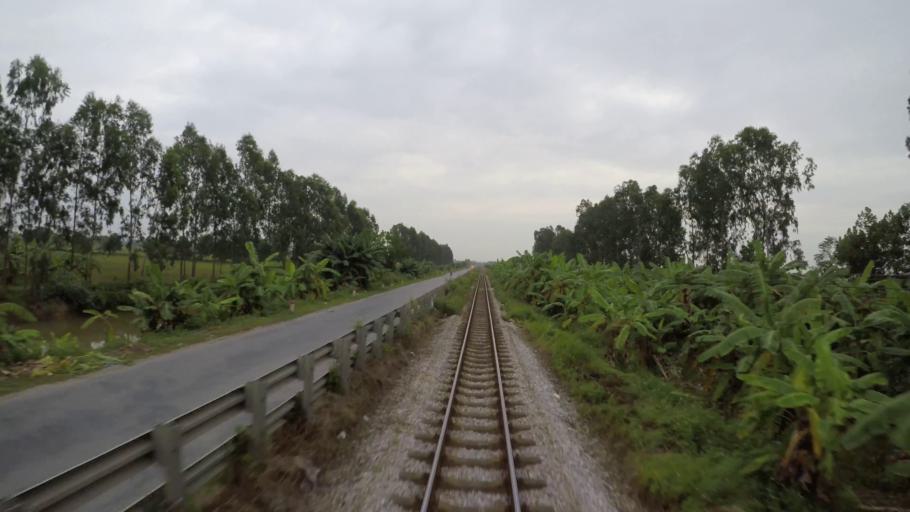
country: VN
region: Hung Yen
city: Ban Yen Nhan
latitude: 20.9852
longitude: 106.0670
